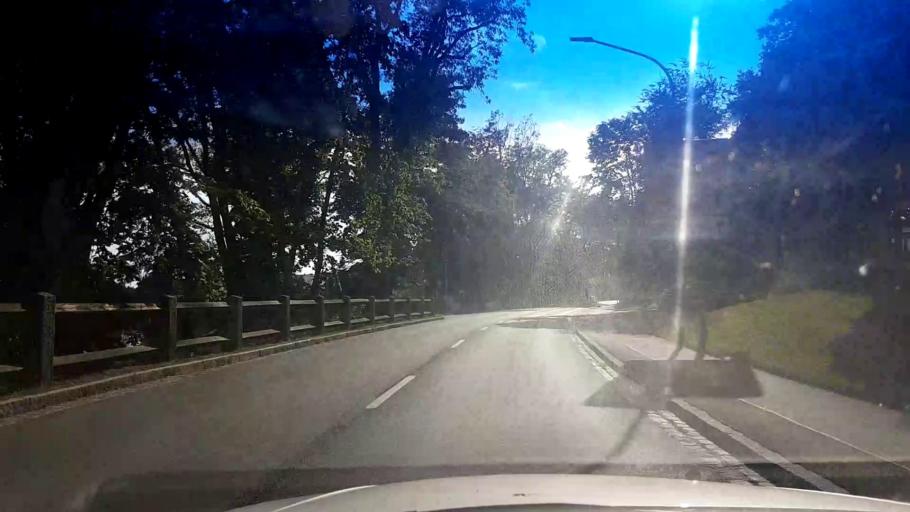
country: DE
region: Bavaria
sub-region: Upper Palatinate
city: Tirschenreuth
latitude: 49.8809
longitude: 12.3431
